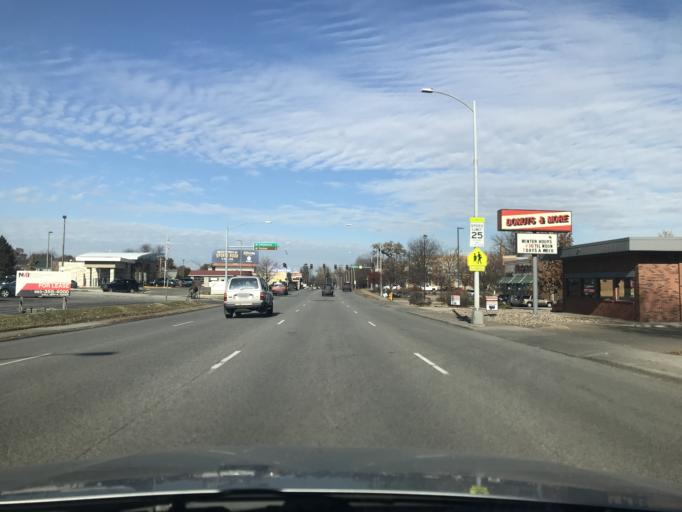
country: US
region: Iowa
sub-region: Scott County
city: Davenport
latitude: 41.5370
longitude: -90.5740
